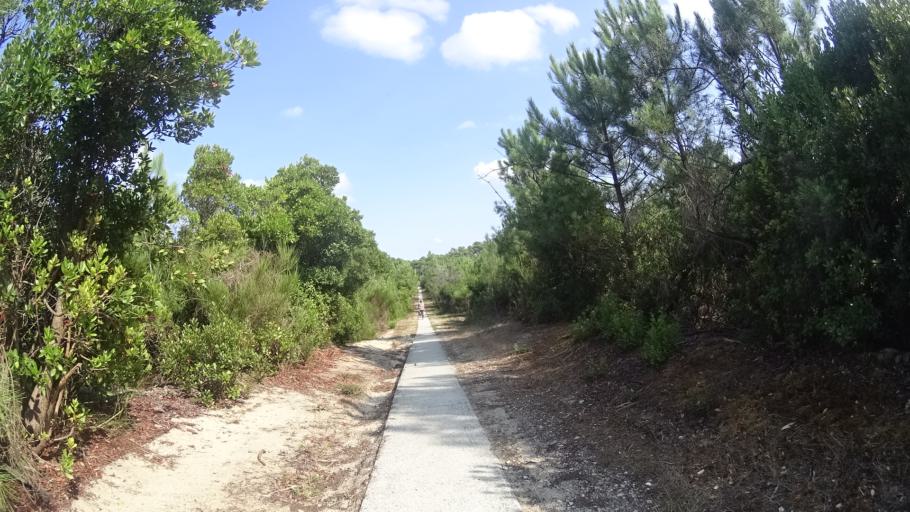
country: FR
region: Aquitaine
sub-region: Departement de la Gironde
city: Lacanau
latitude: 44.9661
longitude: -1.1780
